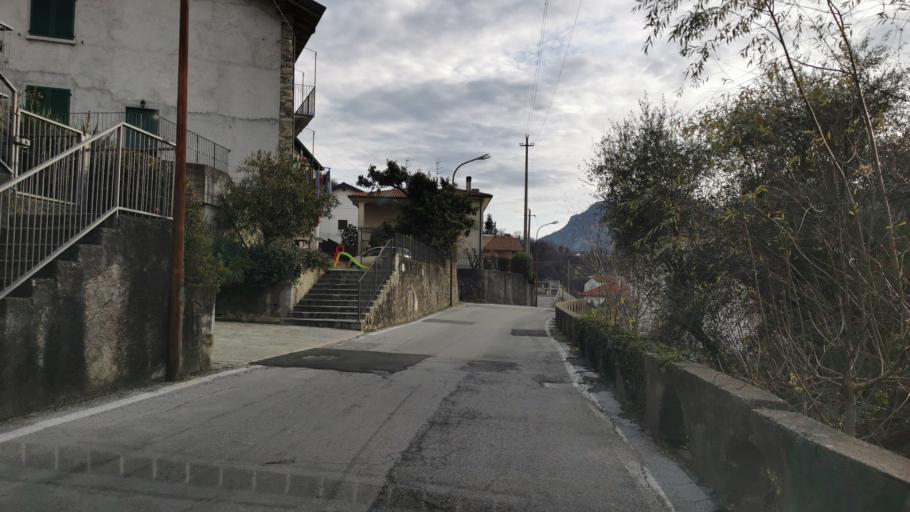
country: IT
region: Lombardy
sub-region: Provincia di Lecco
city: Mandello del Lario
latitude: 45.9242
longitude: 9.3269
